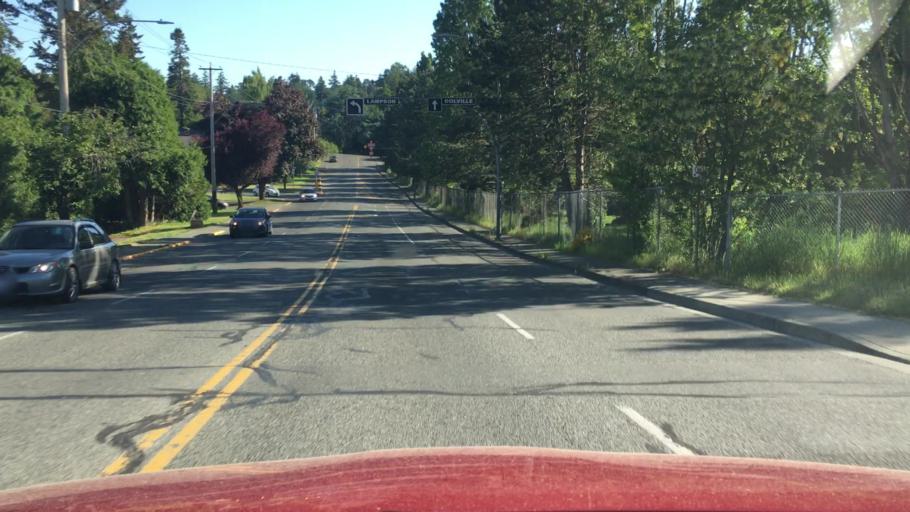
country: CA
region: British Columbia
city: Victoria
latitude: 48.4409
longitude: -123.4026
